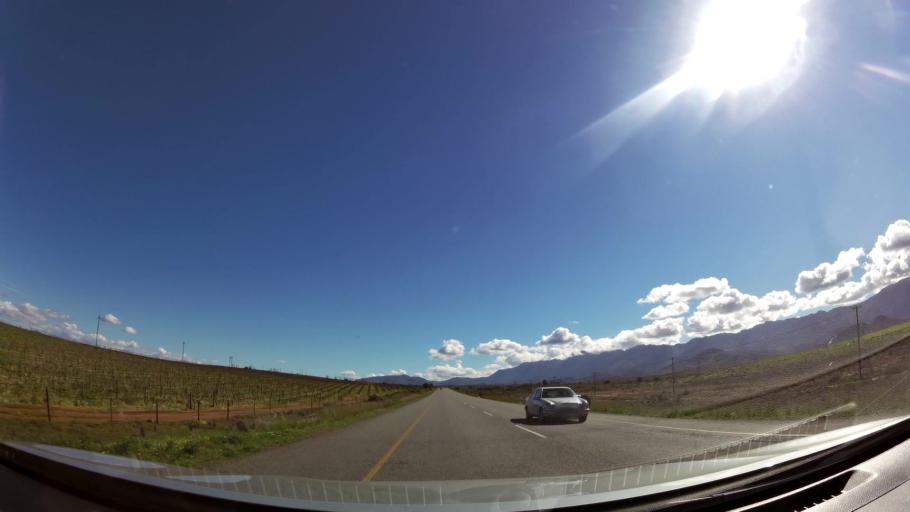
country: ZA
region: Western Cape
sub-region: Cape Winelands District Municipality
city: Ashton
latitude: -33.8317
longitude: 19.9949
